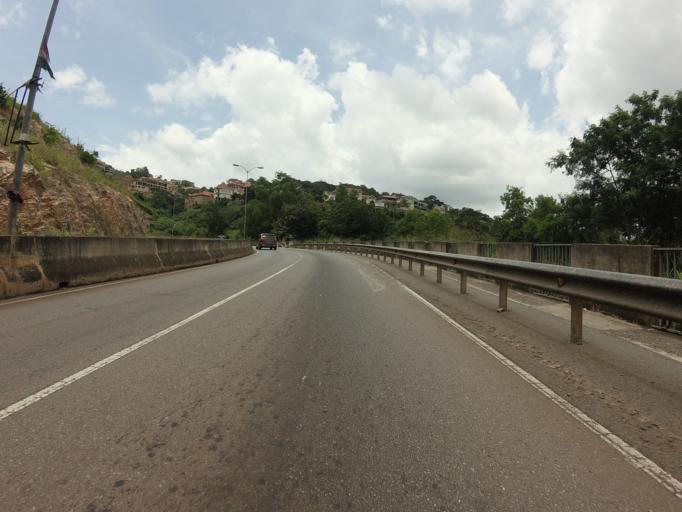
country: GH
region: Eastern
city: Aburi
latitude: 5.7930
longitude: -0.1863
